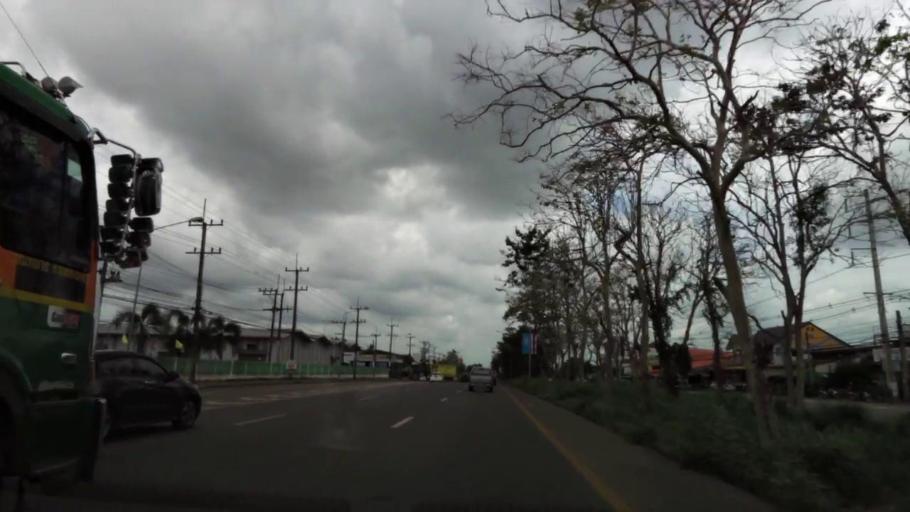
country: TH
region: Rayong
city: Klaeng
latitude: 12.7777
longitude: 101.7078
